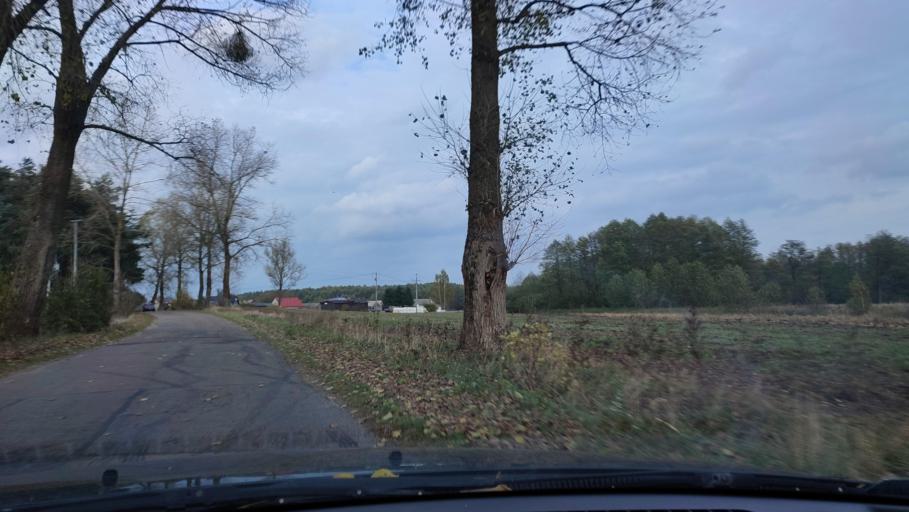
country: PL
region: Masovian Voivodeship
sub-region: Powiat mlawski
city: Mlawa
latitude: 53.1794
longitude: 20.3666
